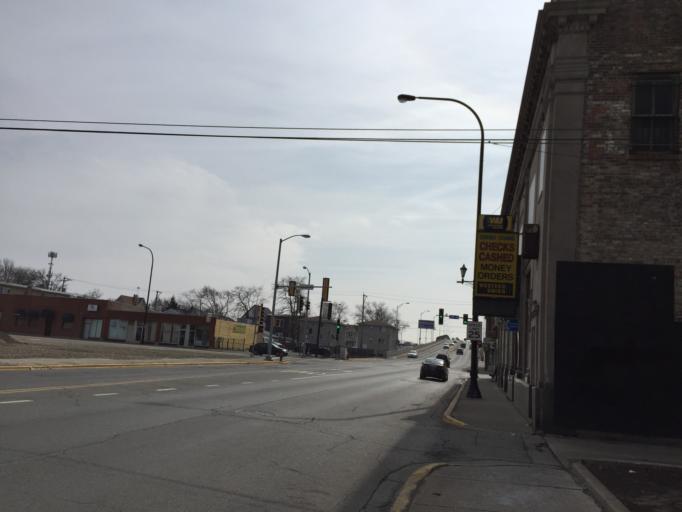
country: US
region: Illinois
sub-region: Cook County
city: Cicero
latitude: 41.8462
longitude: -87.7540
